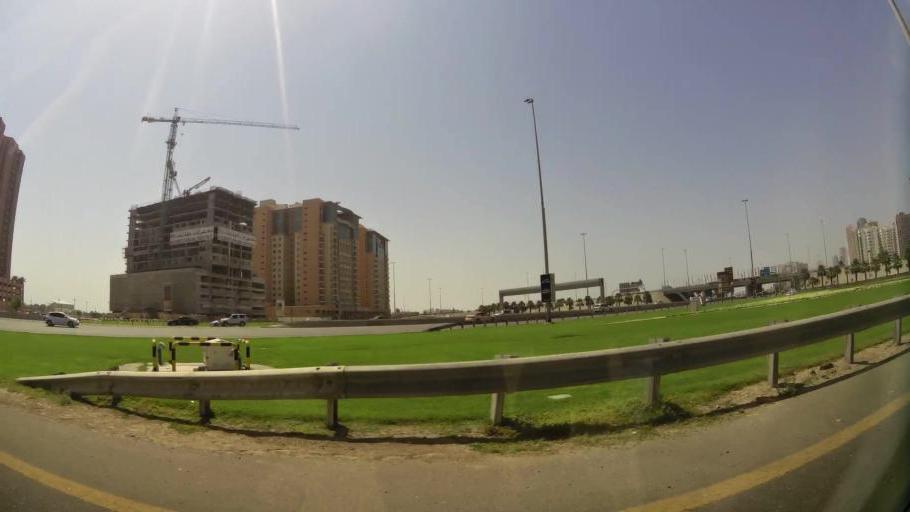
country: AE
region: Ash Shariqah
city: Sharjah
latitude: 25.2879
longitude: 55.3603
